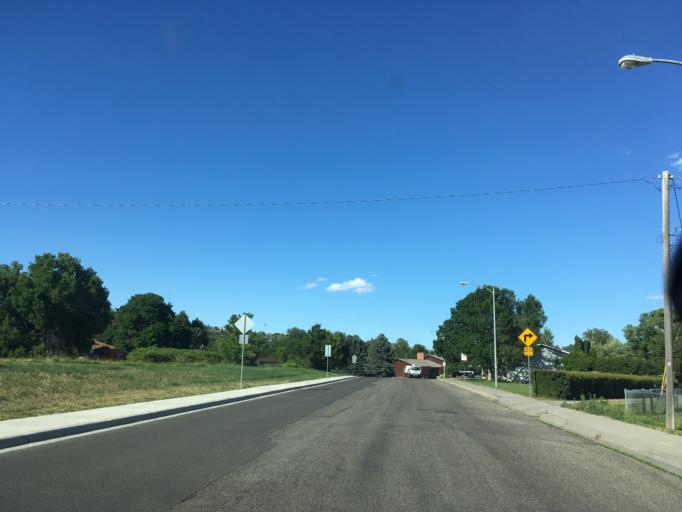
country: US
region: Montana
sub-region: Yellowstone County
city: Billings
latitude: 45.7894
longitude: -108.5642
